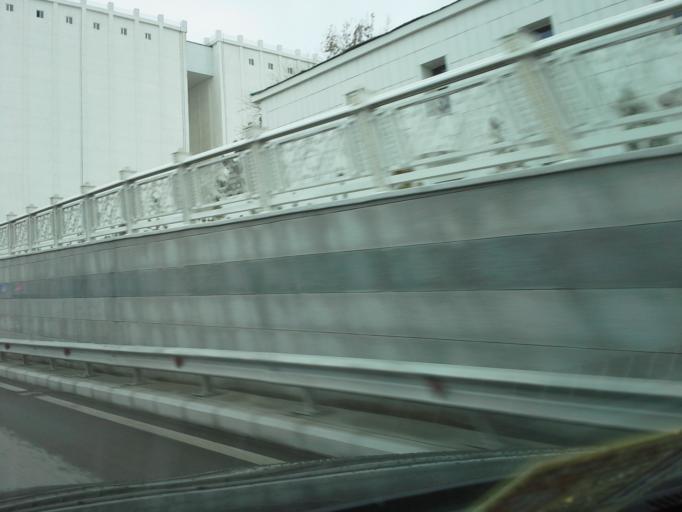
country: TM
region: Ahal
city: Ashgabat
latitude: 37.9562
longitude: 58.3752
